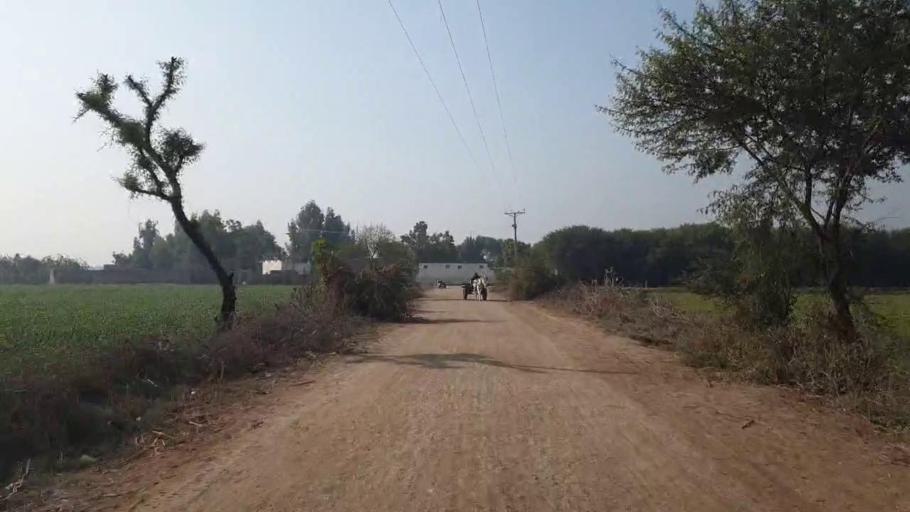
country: PK
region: Sindh
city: Matiari
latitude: 25.6753
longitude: 68.4962
